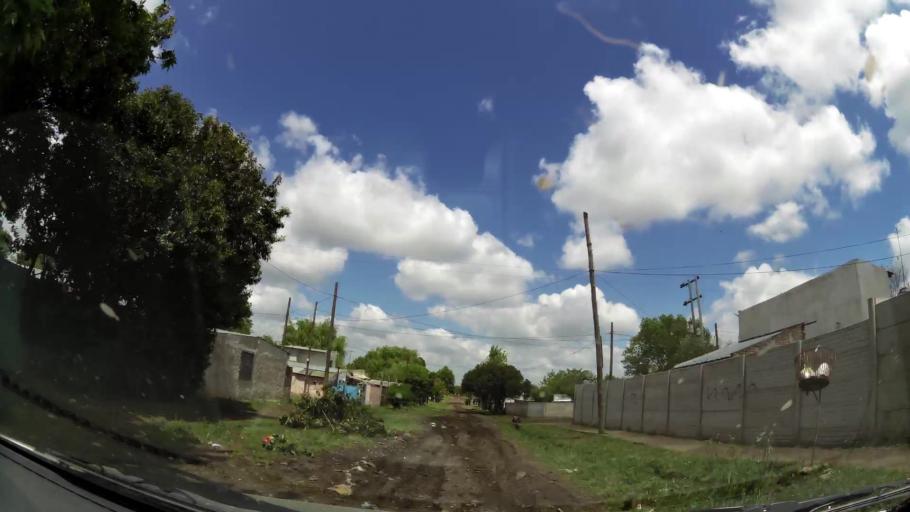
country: AR
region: Buenos Aires
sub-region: Partido de Quilmes
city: Quilmes
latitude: -34.8409
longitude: -58.2300
